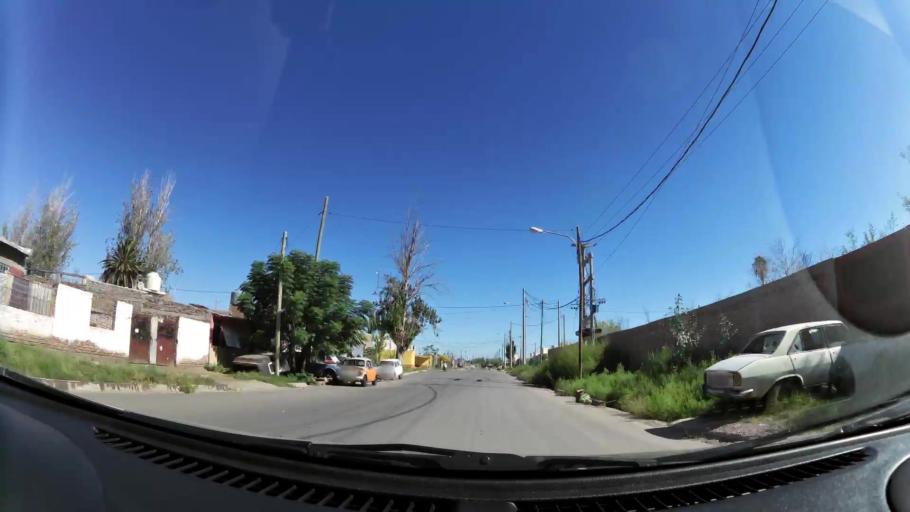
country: AR
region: Mendoza
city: Las Heras
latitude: -32.8318
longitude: -68.8171
